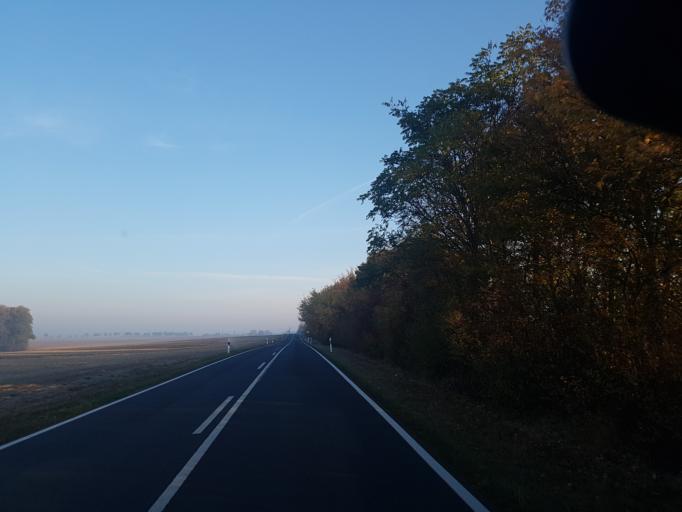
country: DE
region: Brandenburg
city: Juterbog
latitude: 51.9302
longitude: 13.0875
